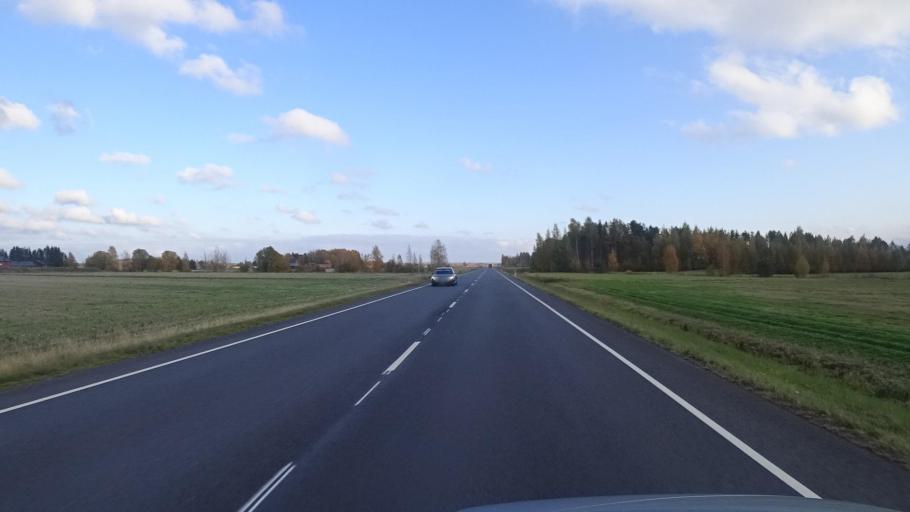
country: FI
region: Satakunta
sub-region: Rauma
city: Koeylioe
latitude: 61.0742
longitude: 22.2981
